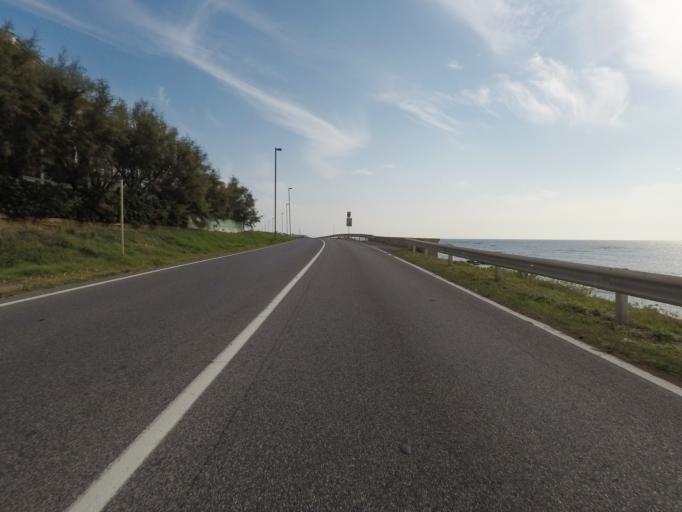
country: IT
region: Latium
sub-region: Citta metropolitana di Roma Capitale
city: Santa Marinella
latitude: 42.0426
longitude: 11.8275
